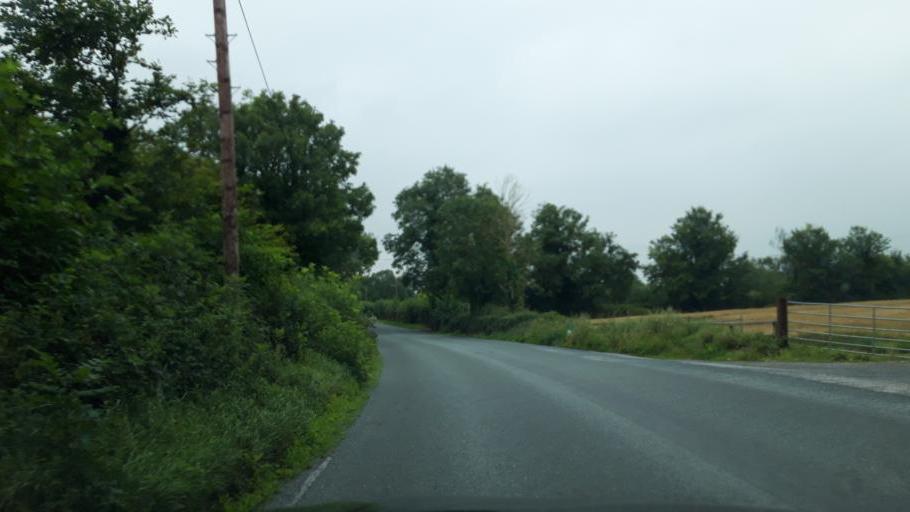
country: IE
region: Munster
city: Fethard
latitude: 52.4483
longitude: -7.7031
